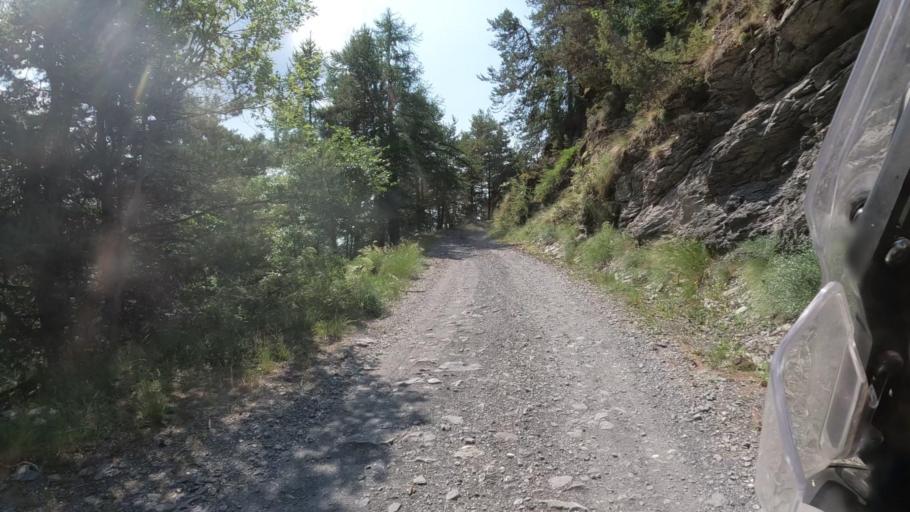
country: IT
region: Piedmont
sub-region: Provincia di Cuneo
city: Briga Alta
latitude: 44.0404
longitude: 7.7013
